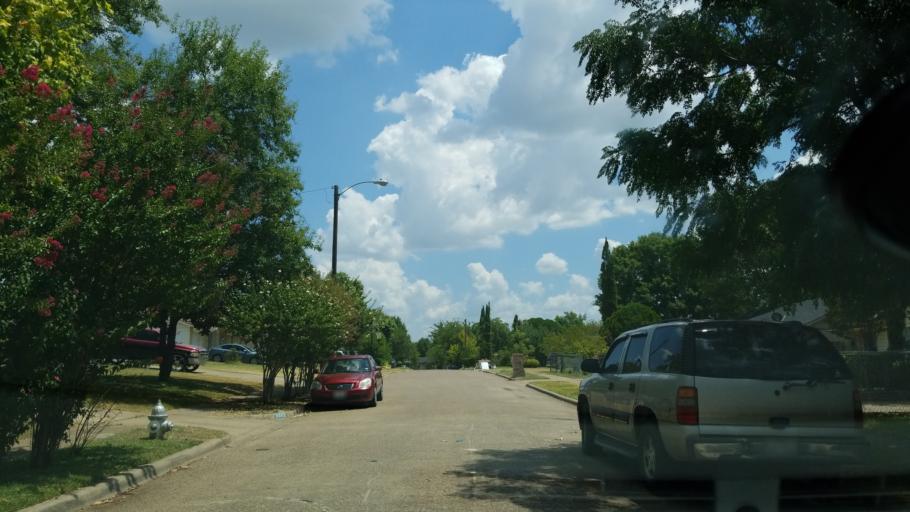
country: US
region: Texas
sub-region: Dallas County
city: Cockrell Hill
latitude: 32.7165
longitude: -96.8987
